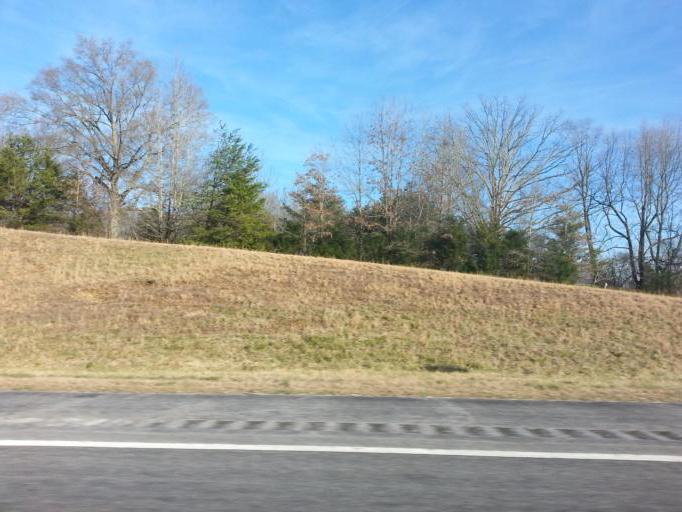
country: US
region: Tennessee
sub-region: Van Buren County
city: Spencer
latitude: 35.7675
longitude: -85.6248
